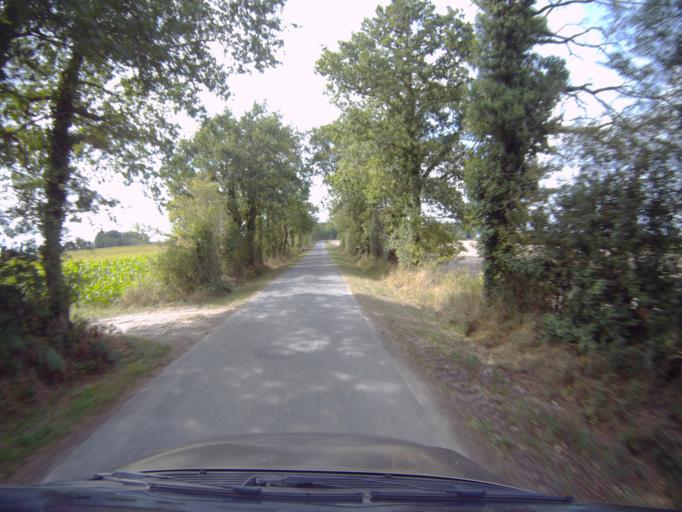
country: FR
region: Pays de la Loire
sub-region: Departement de la Loire-Atlantique
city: La Planche
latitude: 47.0284
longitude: -1.4131
